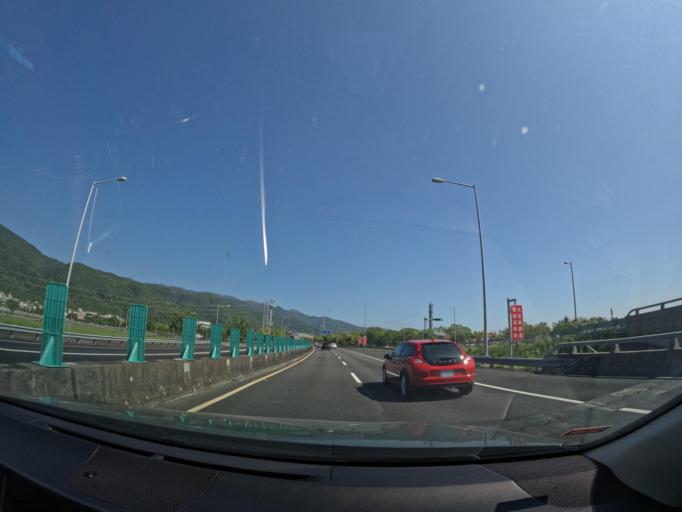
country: TW
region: Taiwan
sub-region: Yilan
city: Yilan
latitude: 24.8288
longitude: 121.7876
